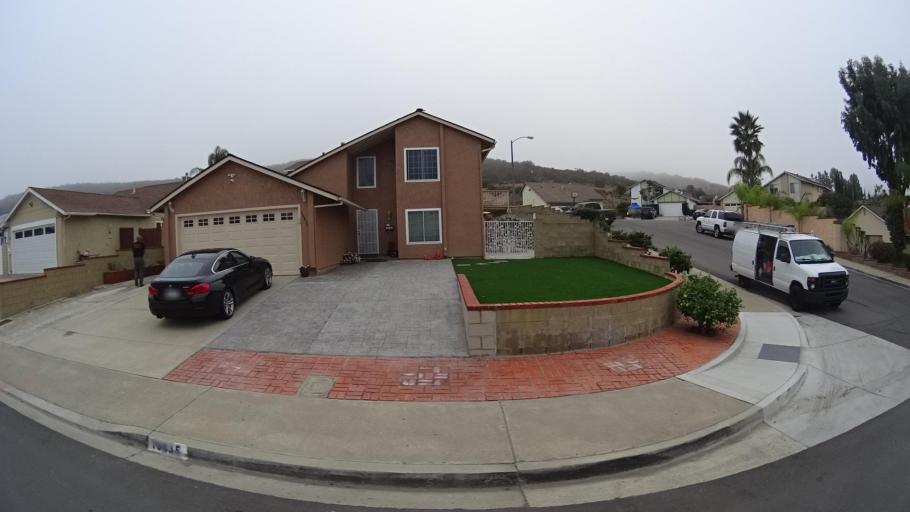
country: US
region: California
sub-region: San Diego County
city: Rancho San Diego
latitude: 32.7290
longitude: -116.9570
